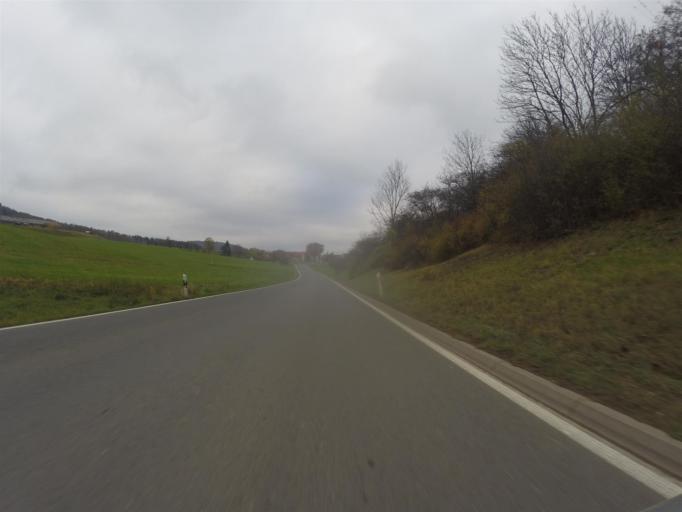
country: DE
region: Thuringia
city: Schongleina
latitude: 50.9261
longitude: 11.7254
